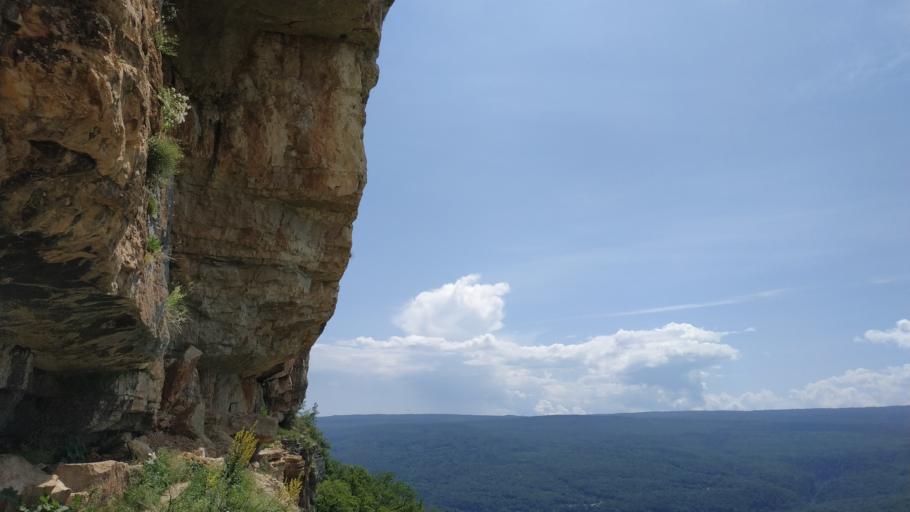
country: RU
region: Adygeya
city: Kamennomostskiy
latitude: 44.2102
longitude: 39.9376
